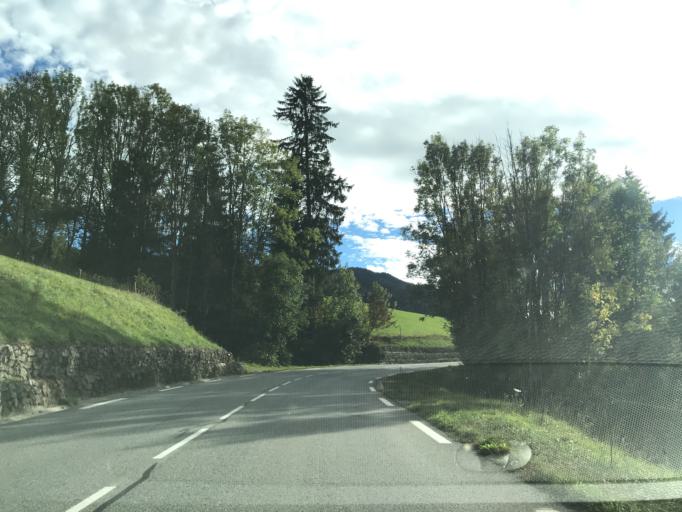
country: FR
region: Rhone-Alpes
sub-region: Departement de la Haute-Savoie
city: Saint-Jean-de-Sixt
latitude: 45.9268
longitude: 6.4118
